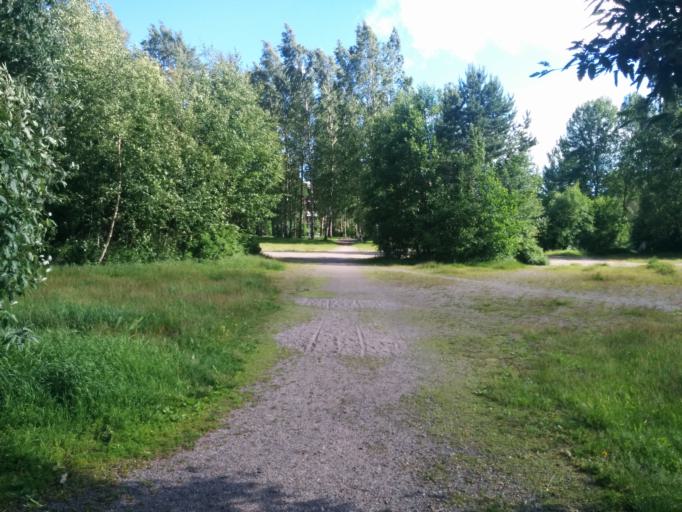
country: FI
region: Uusimaa
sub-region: Helsinki
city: Vantaa
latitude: 60.2448
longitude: 25.1123
